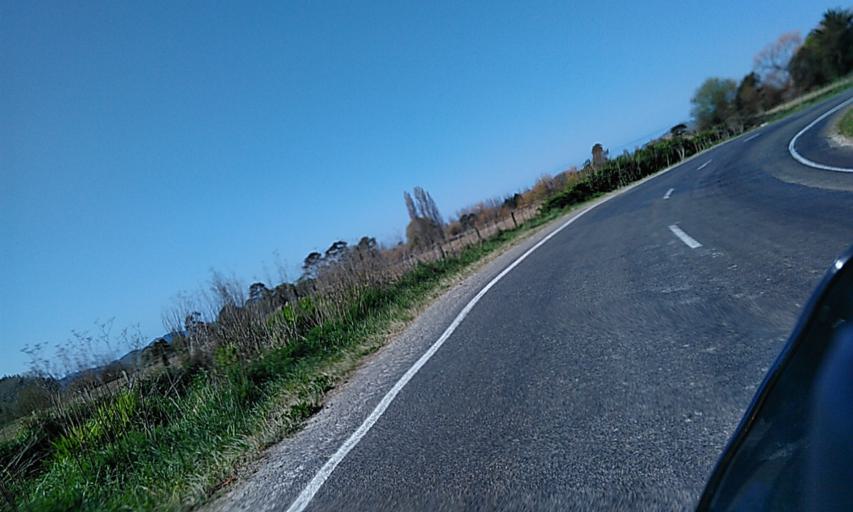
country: NZ
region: Gisborne
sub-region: Gisborne District
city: Gisborne
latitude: -38.3536
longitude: 178.2408
